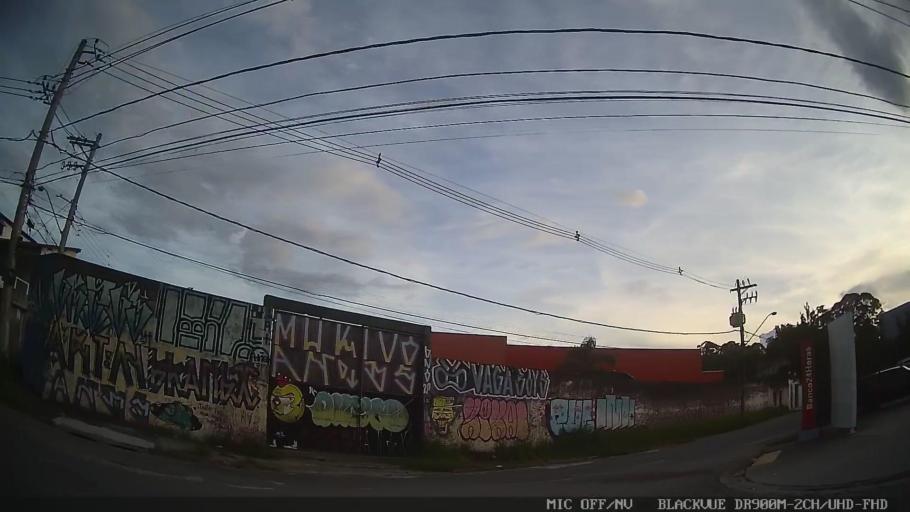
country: BR
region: Sao Paulo
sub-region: Mogi das Cruzes
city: Mogi das Cruzes
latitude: -23.4997
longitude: -46.1870
